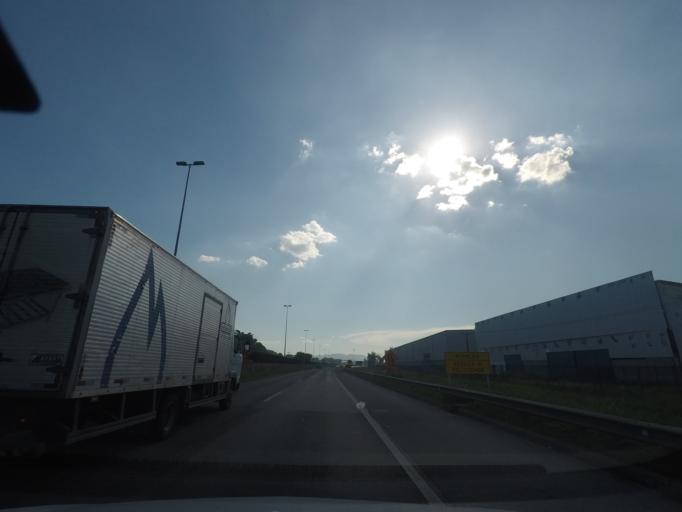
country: BR
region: Rio de Janeiro
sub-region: Duque De Caxias
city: Duque de Caxias
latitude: -22.6634
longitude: -43.2573
